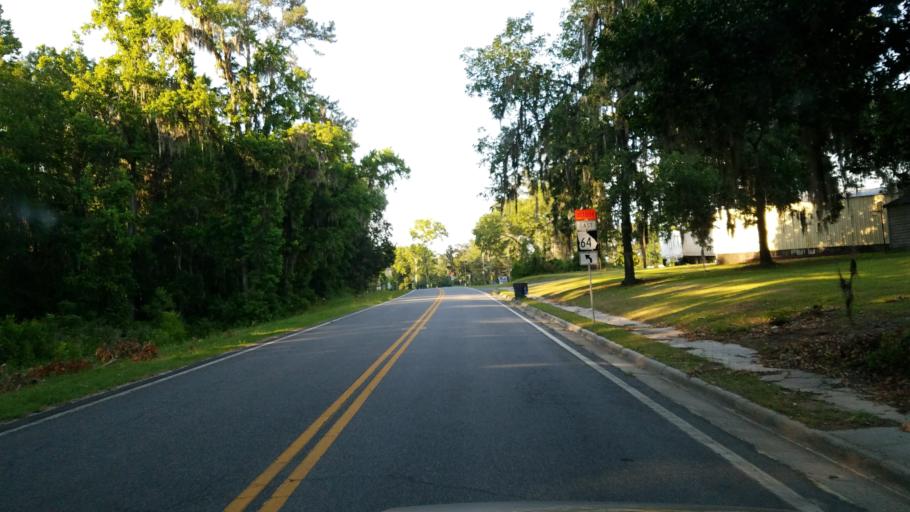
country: US
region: Georgia
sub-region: Lanier County
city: Lakeland
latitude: 31.0443
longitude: -83.0718
